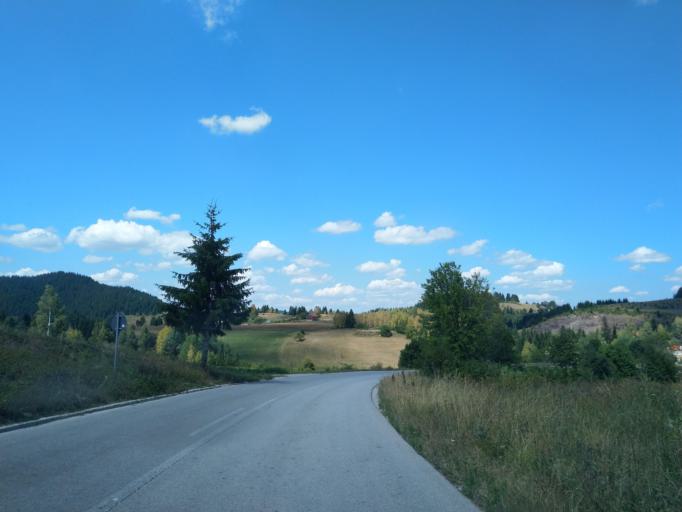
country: RS
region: Central Serbia
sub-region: Zlatiborski Okrug
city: Nova Varos
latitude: 43.4236
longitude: 19.8271
